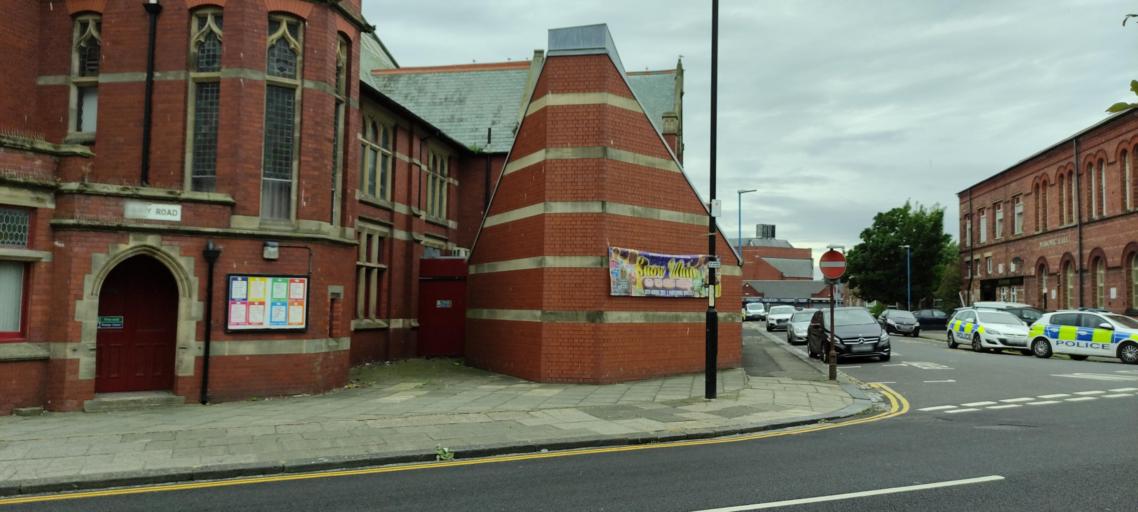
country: GB
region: England
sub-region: Hartlepool
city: Hartlepool
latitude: 54.6865
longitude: -1.2133
